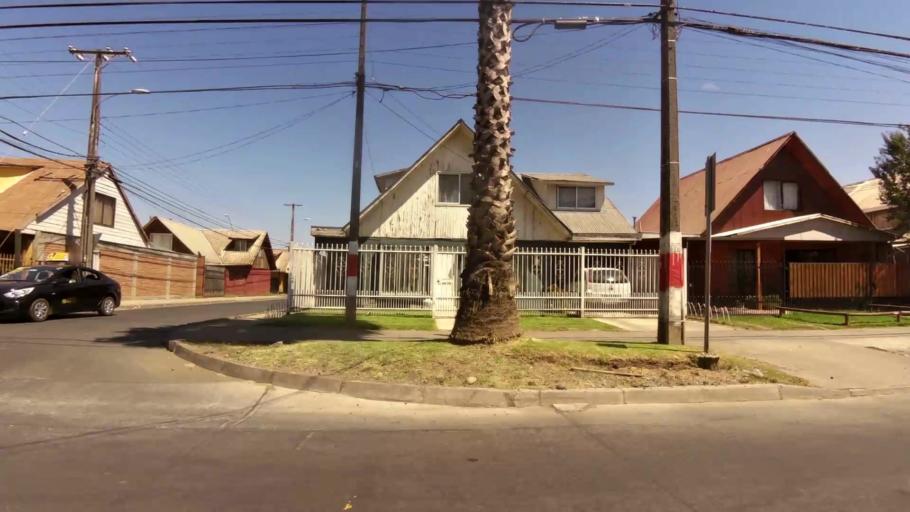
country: CL
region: Maule
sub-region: Provincia de Curico
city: Curico
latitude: -34.9685
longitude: -71.2304
